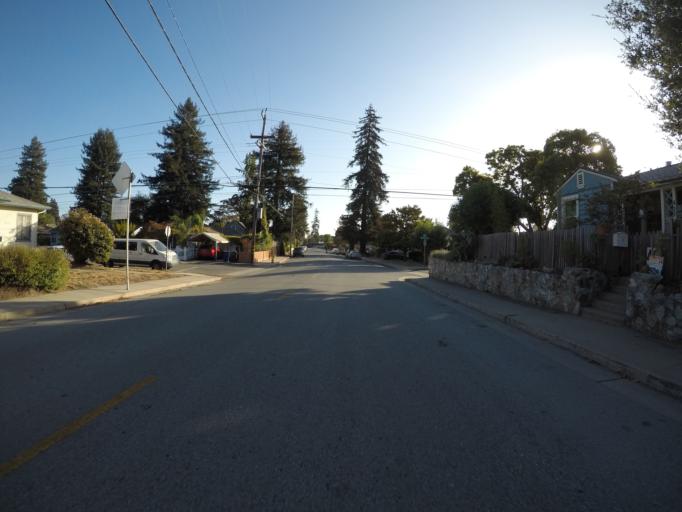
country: US
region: California
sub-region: Santa Cruz County
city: Santa Cruz
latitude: 36.9871
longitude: -122.0186
